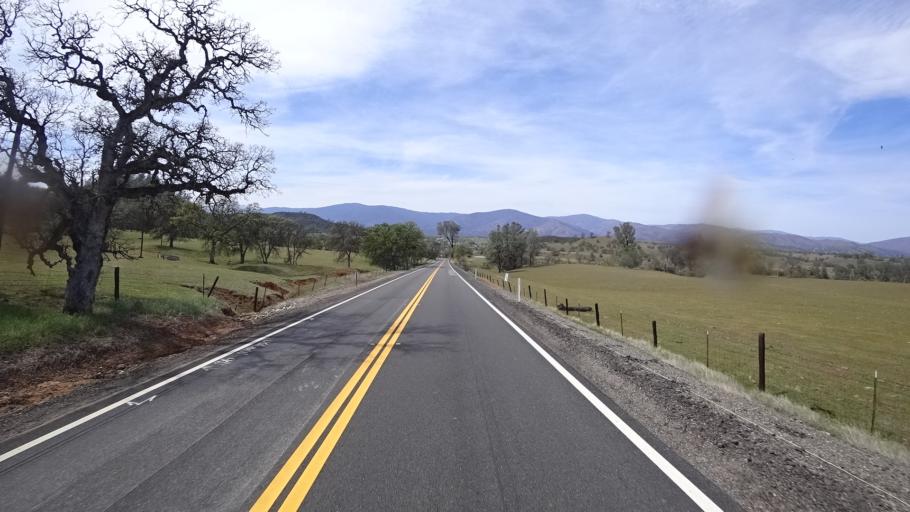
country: US
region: California
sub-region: Glenn County
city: Willows
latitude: 39.6154
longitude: -122.5146
